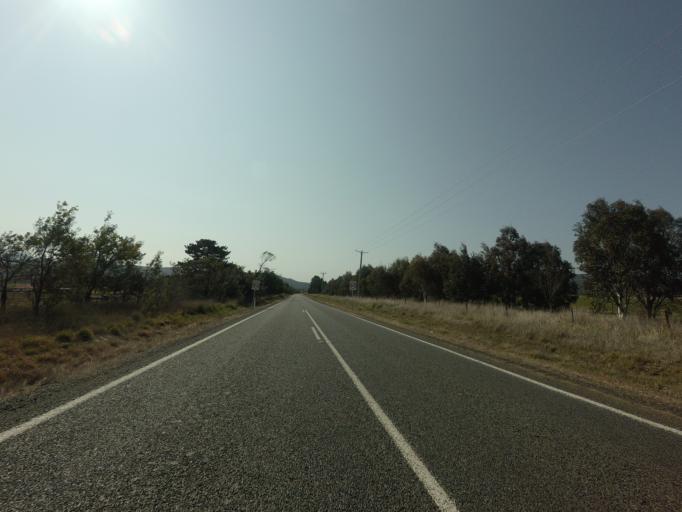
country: AU
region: Tasmania
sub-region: Northern Midlands
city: Evandale
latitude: -41.7889
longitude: 147.7135
